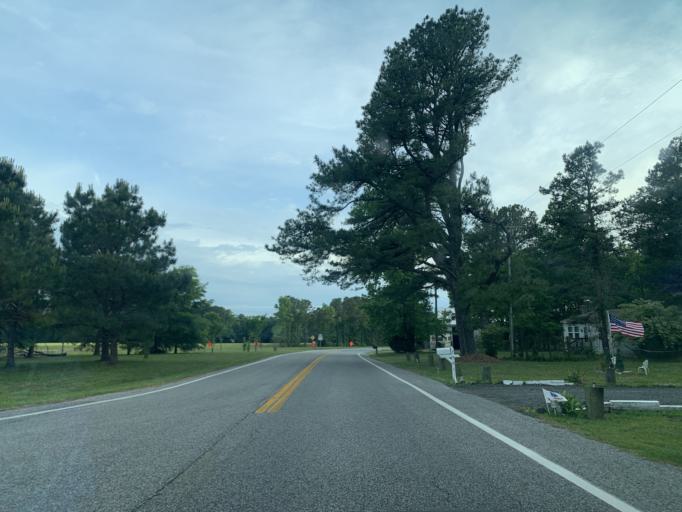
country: US
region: Maryland
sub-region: Worcester County
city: Snow Hill
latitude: 38.1446
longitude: -75.4167
